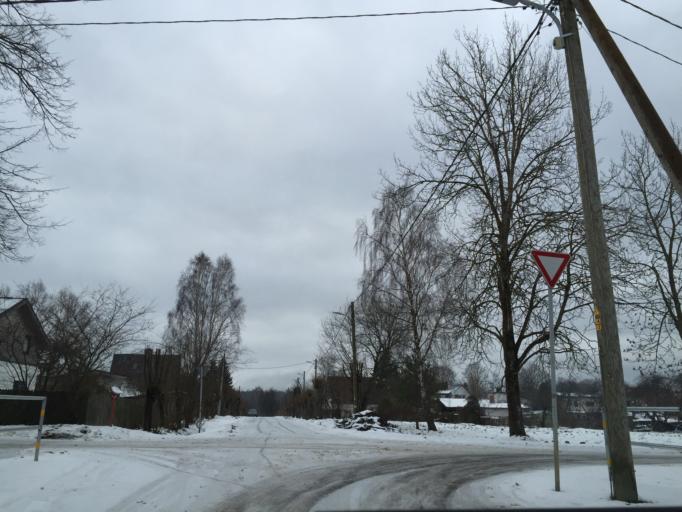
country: LV
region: Saulkrastu
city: Saulkrasti
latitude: 57.2609
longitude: 24.4188
